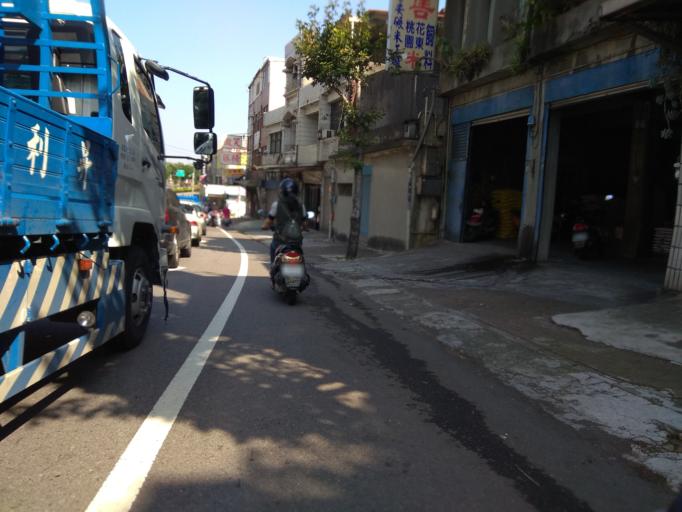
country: TW
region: Taiwan
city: Daxi
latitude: 24.9229
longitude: 121.1874
